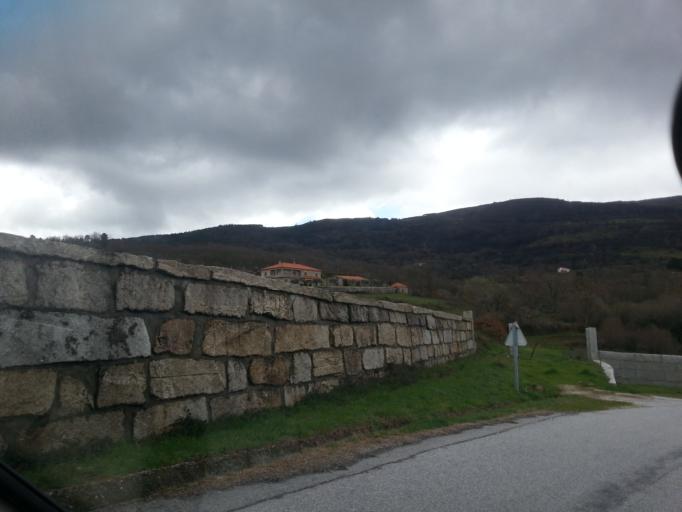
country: PT
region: Guarda
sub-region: Celorico da Beira
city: Celorico da Beira
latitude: 40.5534
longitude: -7.4569
